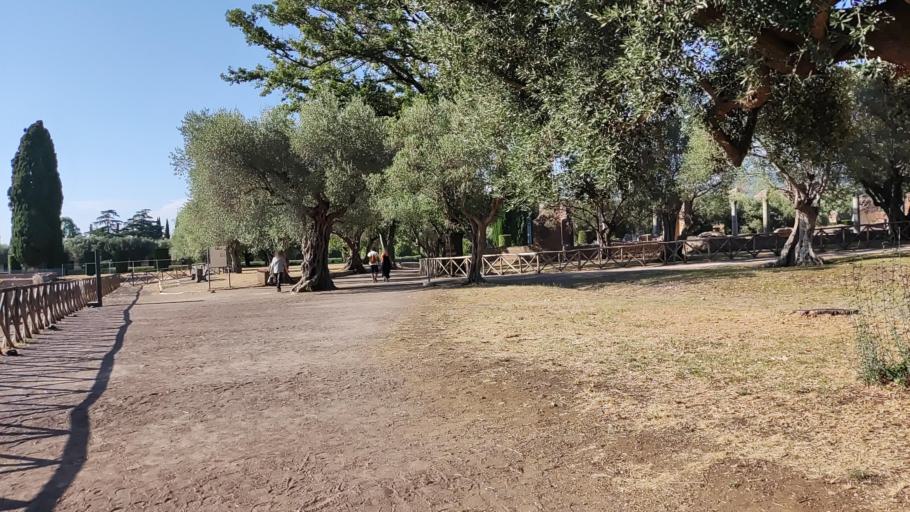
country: IT
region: Latium
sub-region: Citta metropolitana di Roma Capitale
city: Villa Adriana
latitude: 41.9405
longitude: 12.7746
